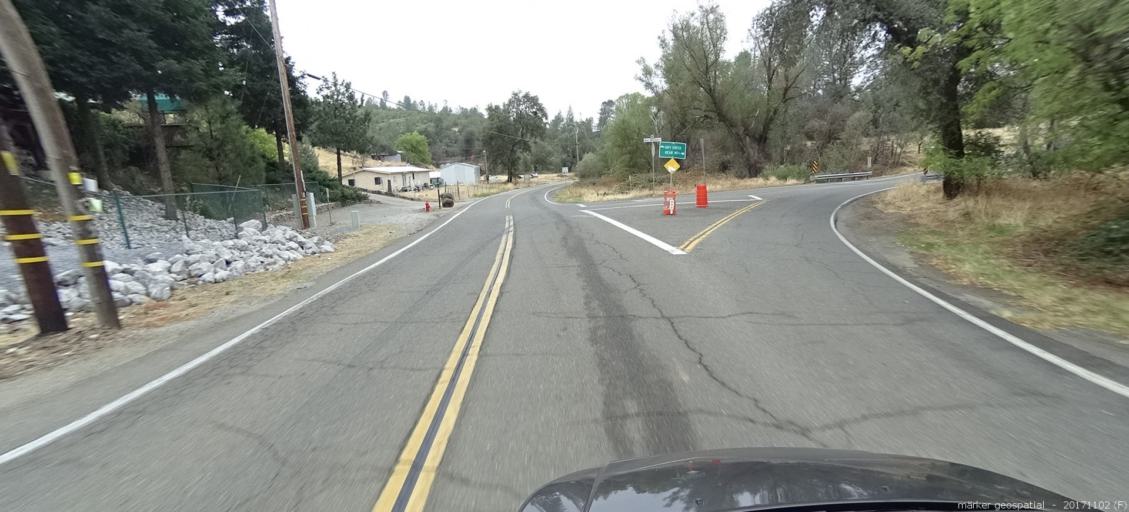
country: US
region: California
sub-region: Shasta County
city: Bella Vista
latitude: 40.7158
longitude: -122.2420
